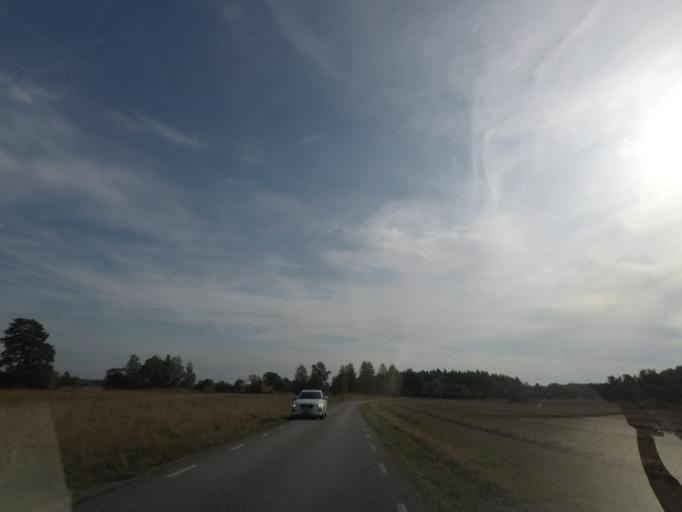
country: SE
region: Vaestmanland
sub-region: Kungsors Kommun
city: Kungsoer
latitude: 59.5233
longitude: 16.1457
